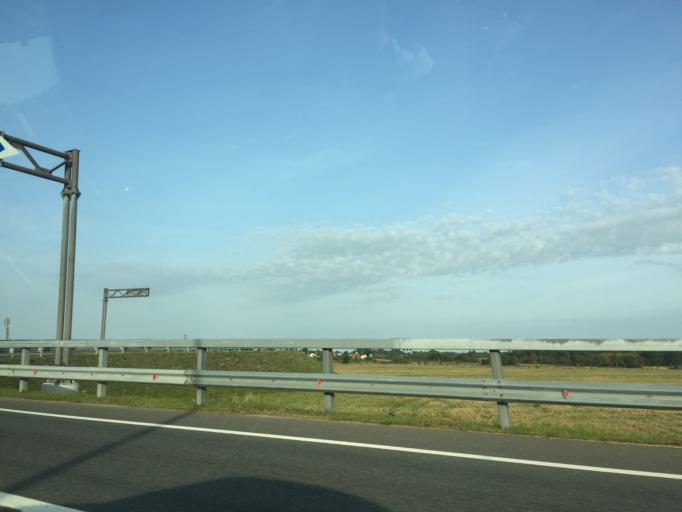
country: RU
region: Kaliningrad
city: Gur'yevsk
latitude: 54.8529
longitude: 20.5680
